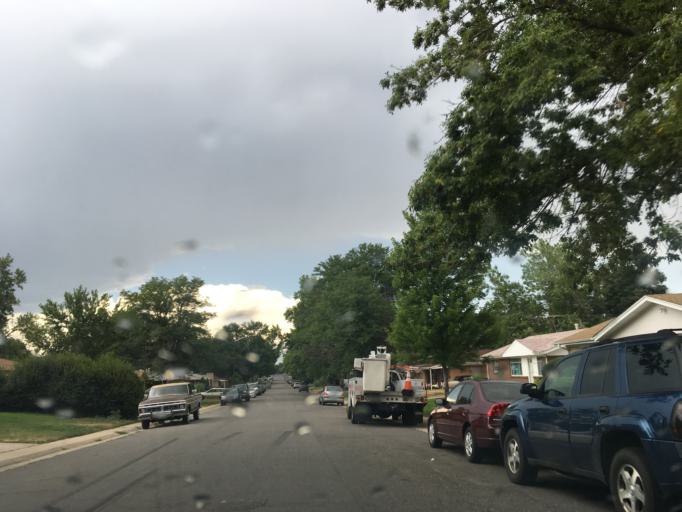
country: US
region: Colorado
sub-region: Arapahoe County
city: Sheridan
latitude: 39.6707
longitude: -105.0407
